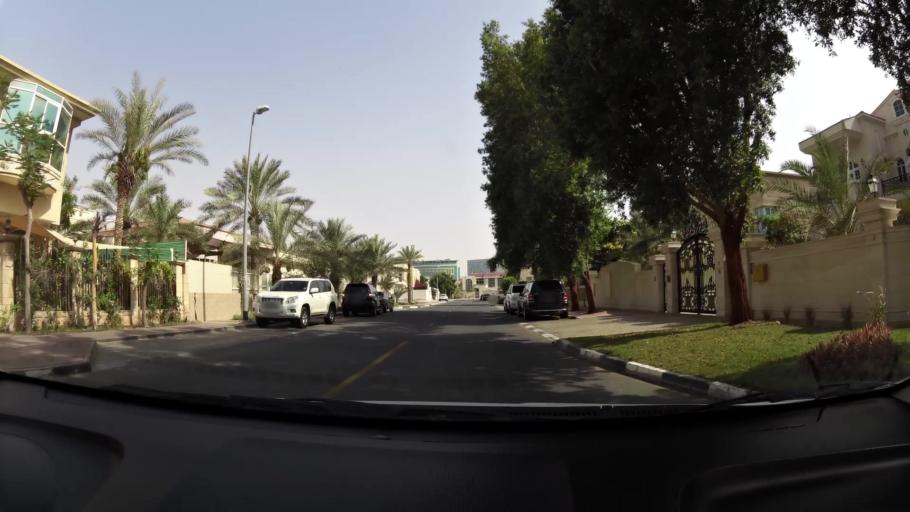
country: AE
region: Ash Shariqah
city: Sharjah
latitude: 25.2398
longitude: 55.3549
